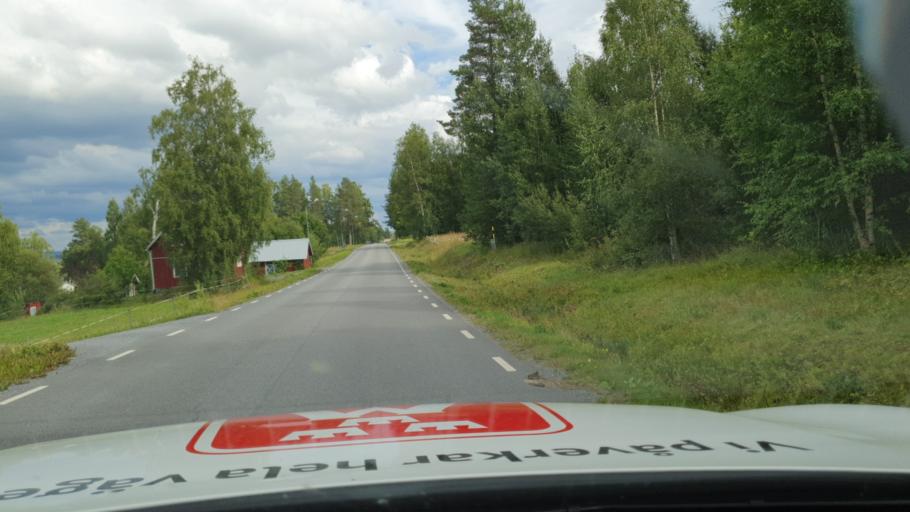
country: SE
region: Jaemtland
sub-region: OEstersunds Kommun
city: Lit
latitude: 63.3076
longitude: 14.8630
